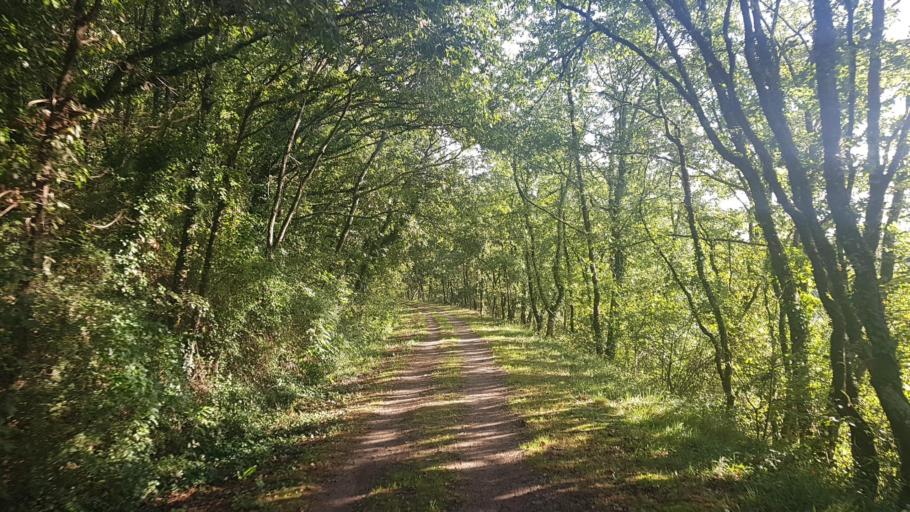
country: FR
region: Poitou-Charentes
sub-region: Departement de la Vienne
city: Saint-Savin
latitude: 46.5744
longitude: 0.8694
